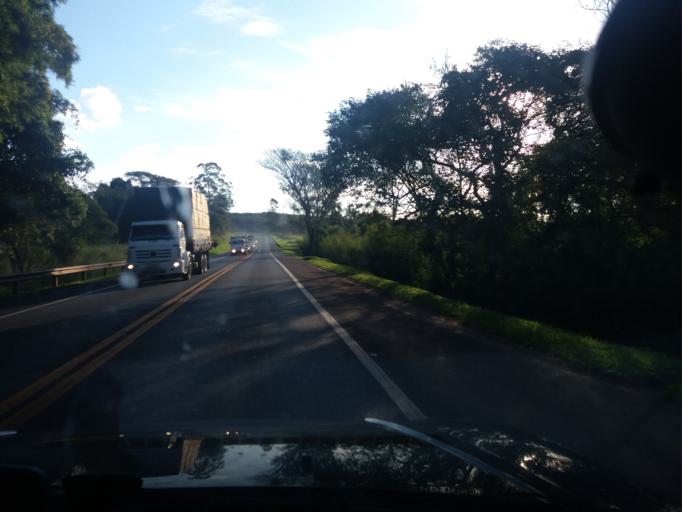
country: BR
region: Sao Paulo
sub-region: Buri
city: Buri
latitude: -23.9279
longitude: -48.6575
